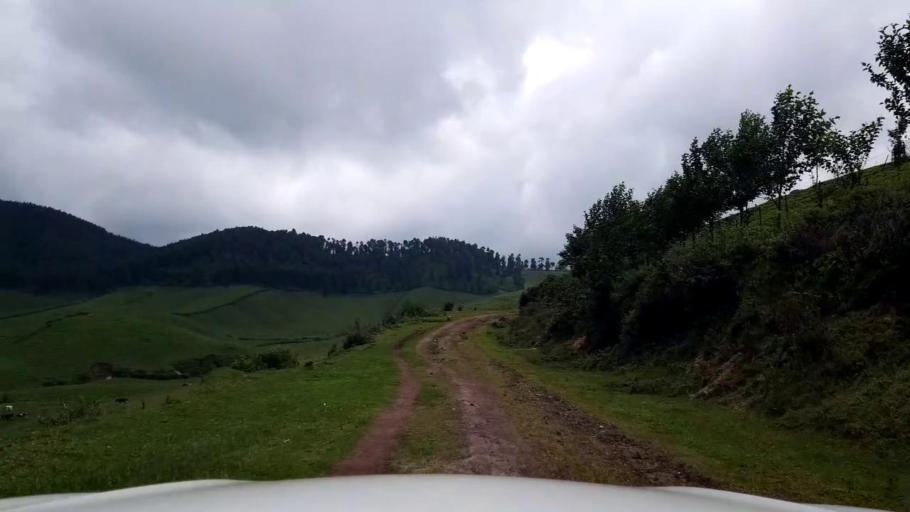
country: RW
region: Western Province
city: Gisenyi
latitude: -1.6882
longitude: 29.4247
